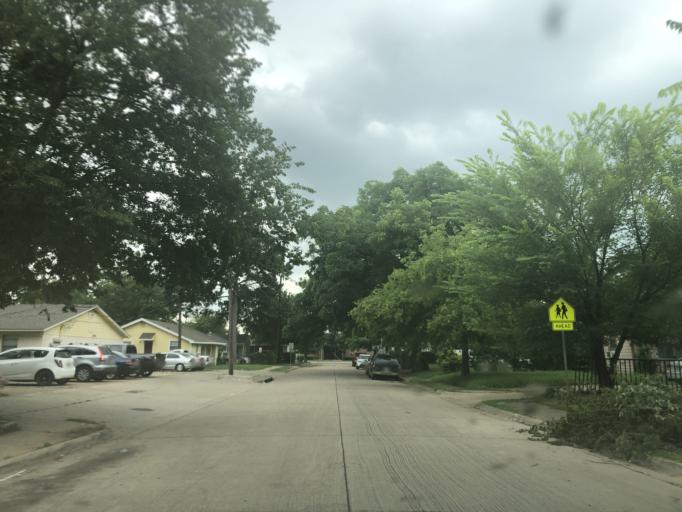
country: US
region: Texas
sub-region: Dallas County
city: Irving
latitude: 32.8098
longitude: -96.9391
